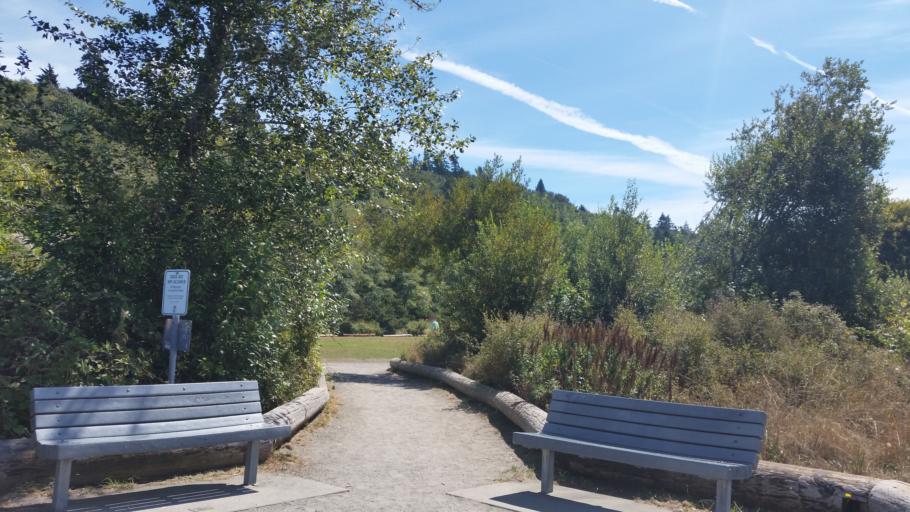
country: US
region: Washington
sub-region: King County
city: Shoreline
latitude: 47.6940
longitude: -122.4054
